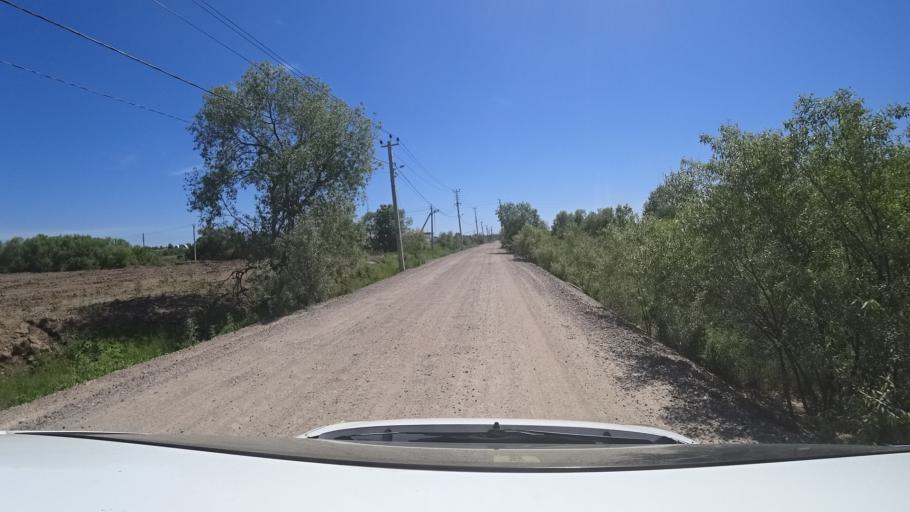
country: RU
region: Khabarovsk Krai
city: Topolevo
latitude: 48.4792
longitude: 135.1732
